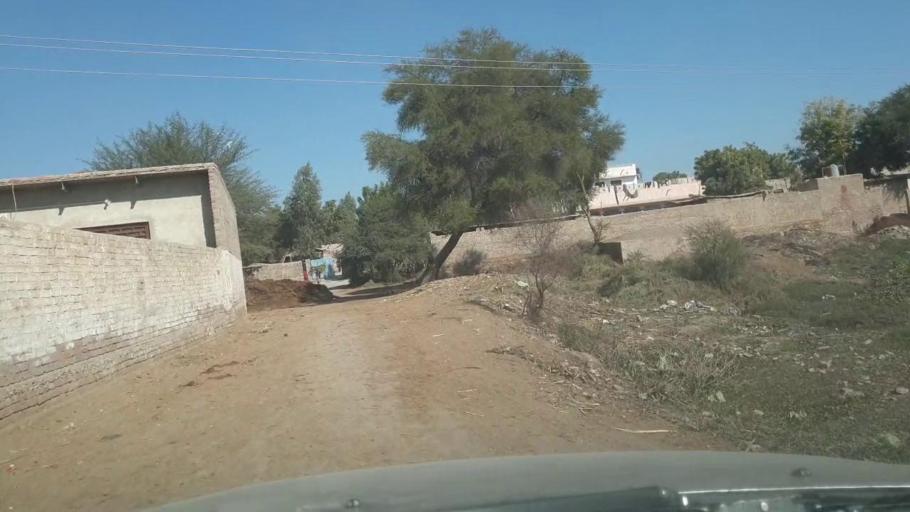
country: PK
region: Sindh
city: Ghotki
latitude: 28.0878
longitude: 69.3410
